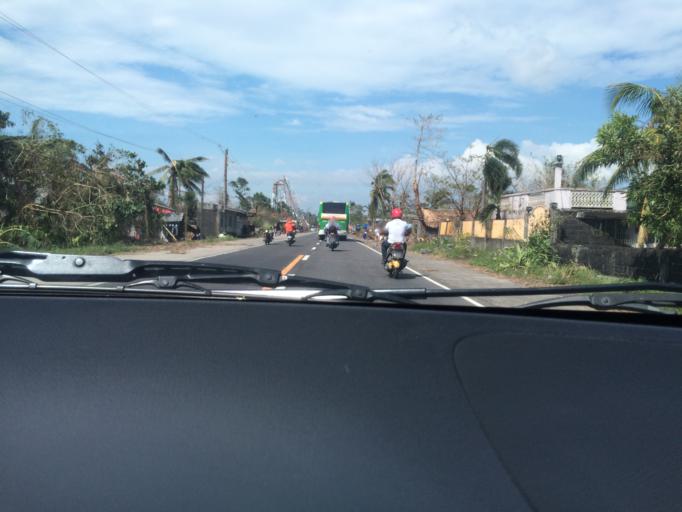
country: PH
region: Bicol
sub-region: Province of Albay
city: Iraya
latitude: 13.2585
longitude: 123.5025
